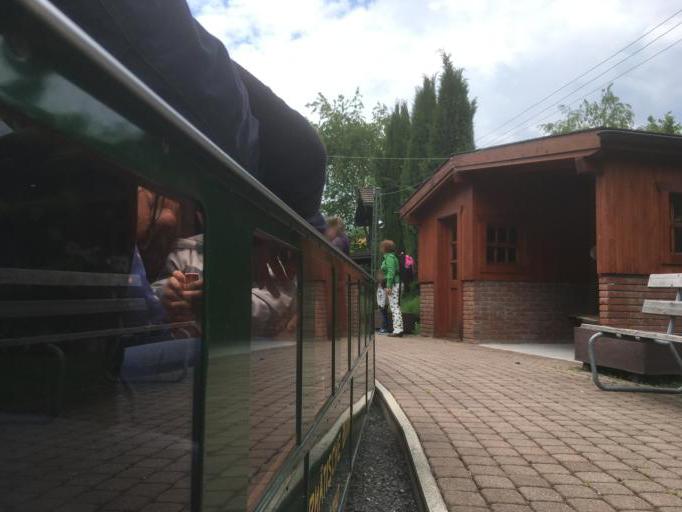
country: CH
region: Valais
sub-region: Monthey District
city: Port-Valais
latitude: 46.3842
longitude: 6.8577
